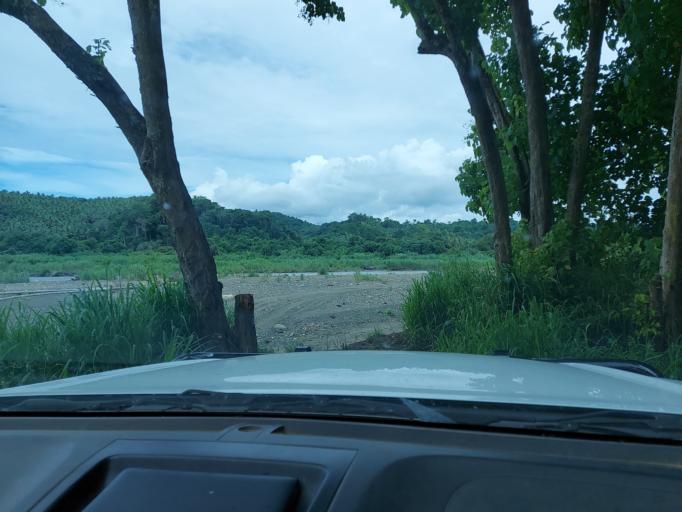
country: VU
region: Malampa
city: Lakatoro
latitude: -16.2745
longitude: 167.6308
